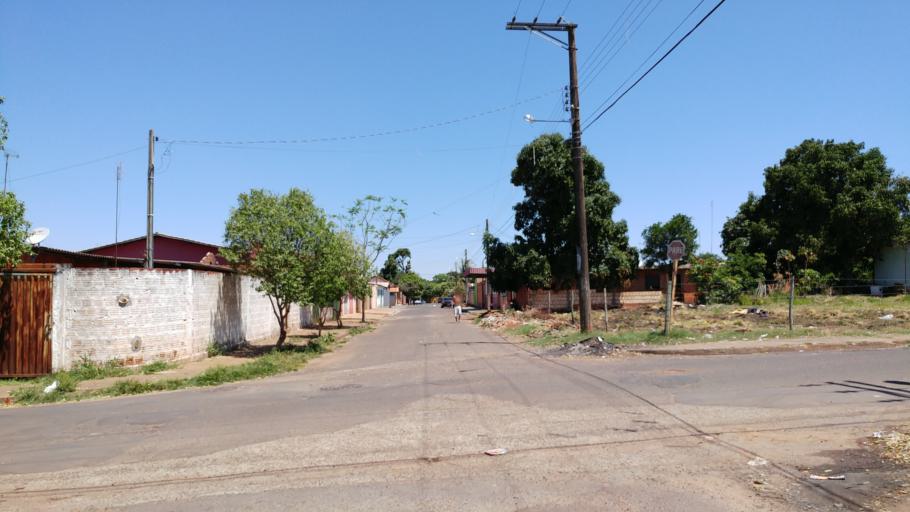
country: BR
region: Sao Paulo
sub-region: Paraguacu Paulista
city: Paraguacu Paulista
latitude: -22.4083
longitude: -50.5688
